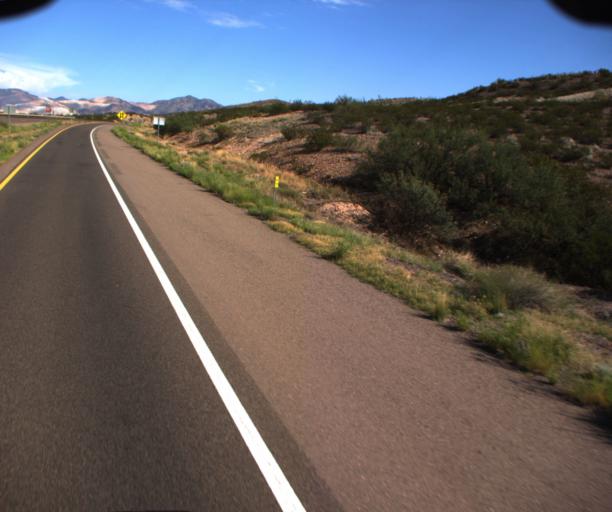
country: US
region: Arizona
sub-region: Greenlee County
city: Clifton
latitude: 33.0076
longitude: -109.2809
